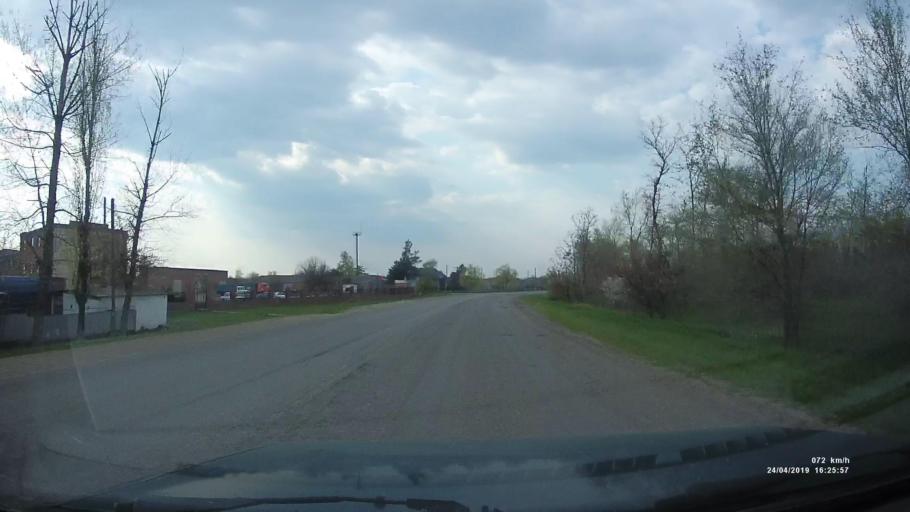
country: RU
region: Rostov
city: Orlovskiy
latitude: 46.8582
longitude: 42.0376
